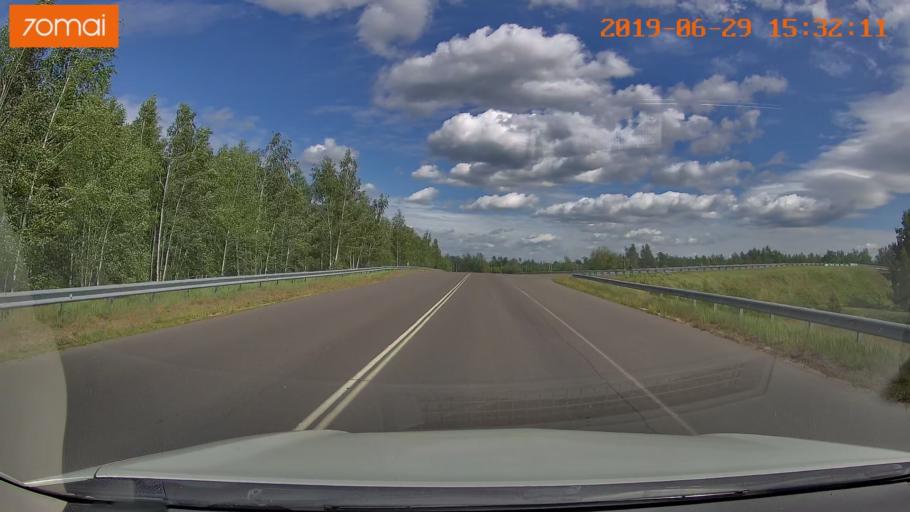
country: BY
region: Brest
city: Mikashevichy
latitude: 52.2104
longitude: 27.4150
